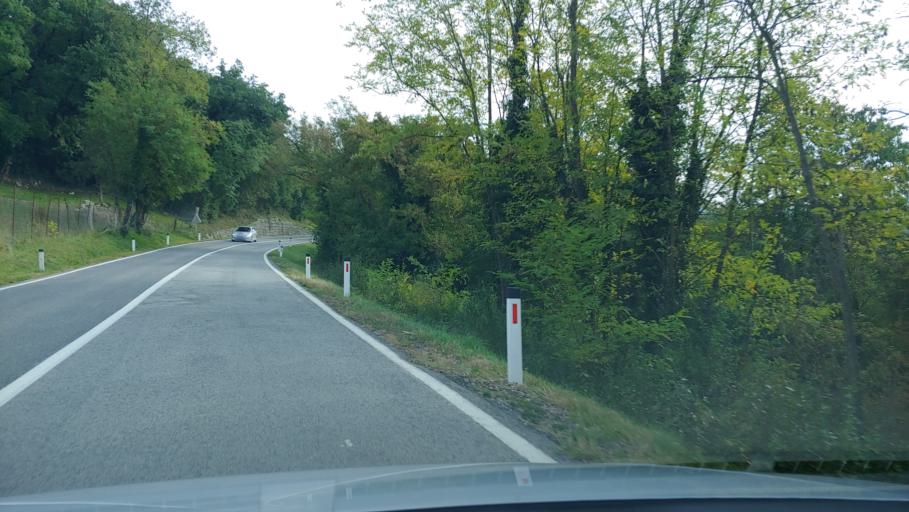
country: SI
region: Nova Gorica
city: Sempas
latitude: 45.9030
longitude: 13.7795
